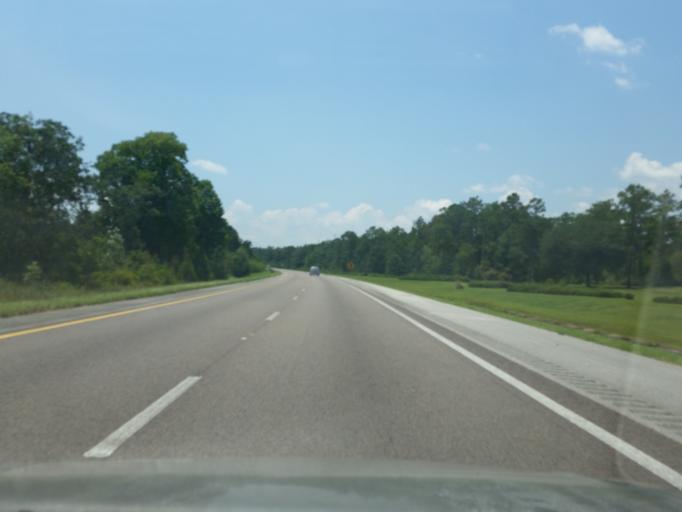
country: US
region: Florida
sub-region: Escambia County
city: Cantonment
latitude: 30.5768
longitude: -87.4220
